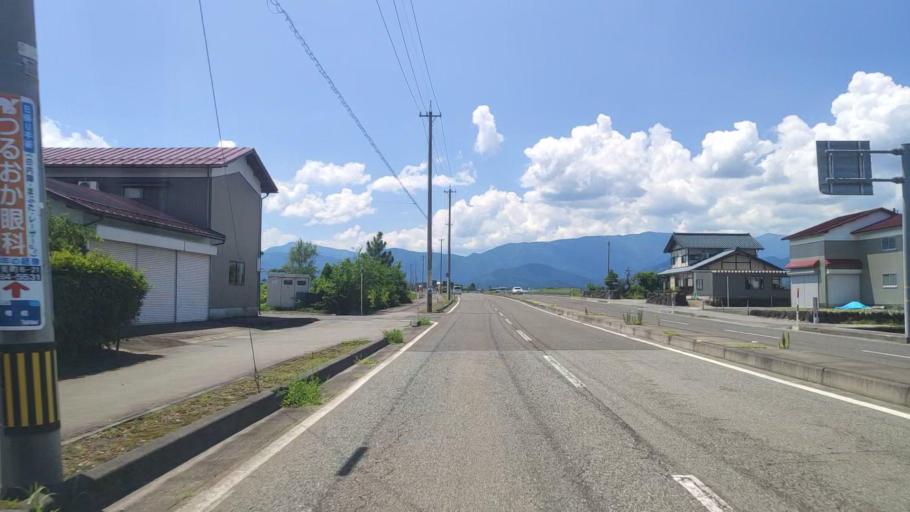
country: JP
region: Fukui
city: Ono
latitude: 36.0018
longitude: 136.5090
